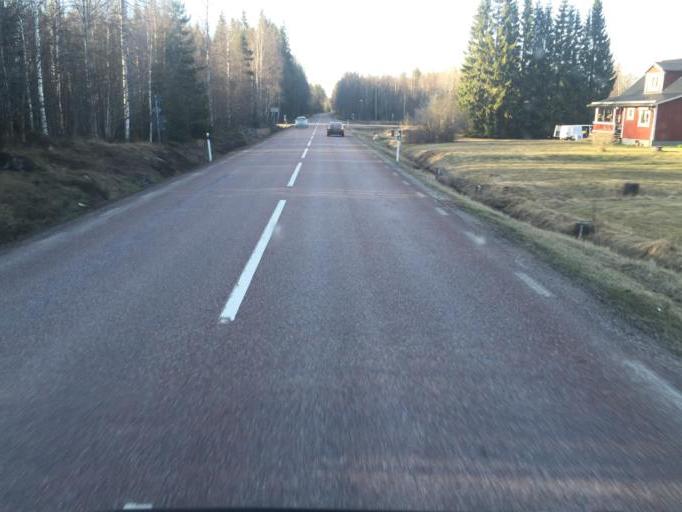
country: SE
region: Dalarna
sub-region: Gagnefs Kommun
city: Mockfjard
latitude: 60.4972
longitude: 14.7834
